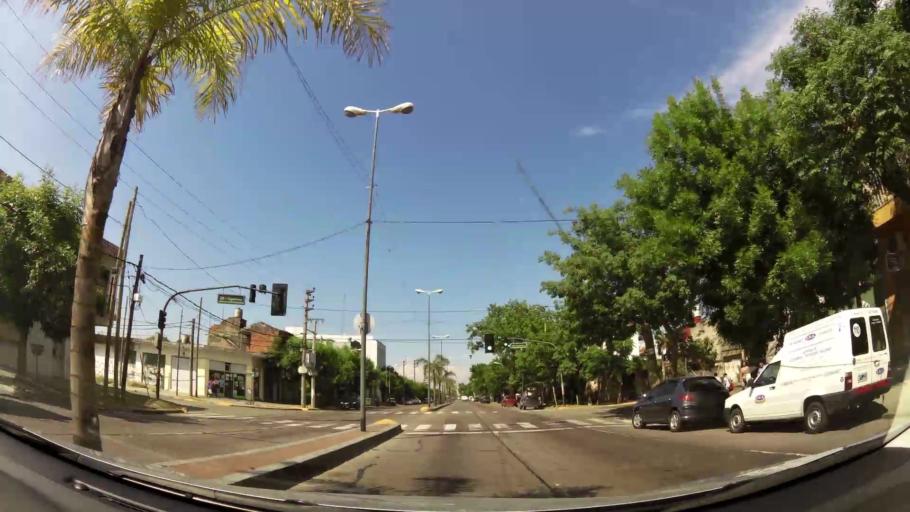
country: AR
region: Buenos Aires
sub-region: Partido de Tigre
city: Tigre
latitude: -34.4685
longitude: -58.5891
